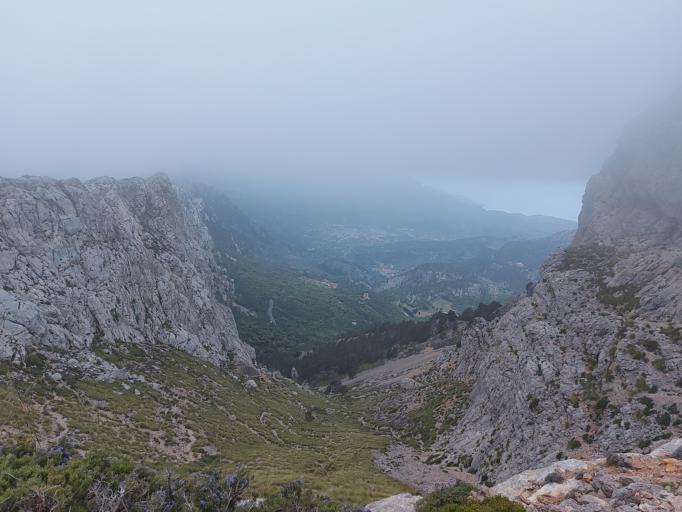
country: ES
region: Balearic Islands
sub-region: Illes Balears
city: Fornalutx
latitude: 39.8000
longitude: 2.7859
